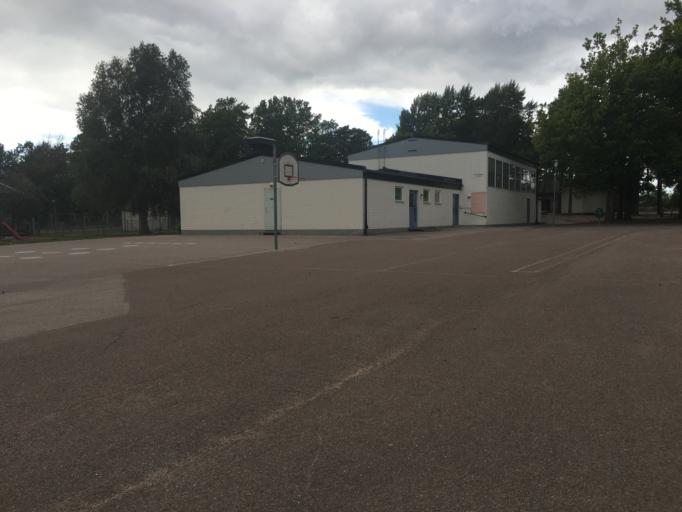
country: SE
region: Kalmar
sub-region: Kalmar Kommun
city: Kalmar
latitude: 56.7000
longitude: 16.3570
